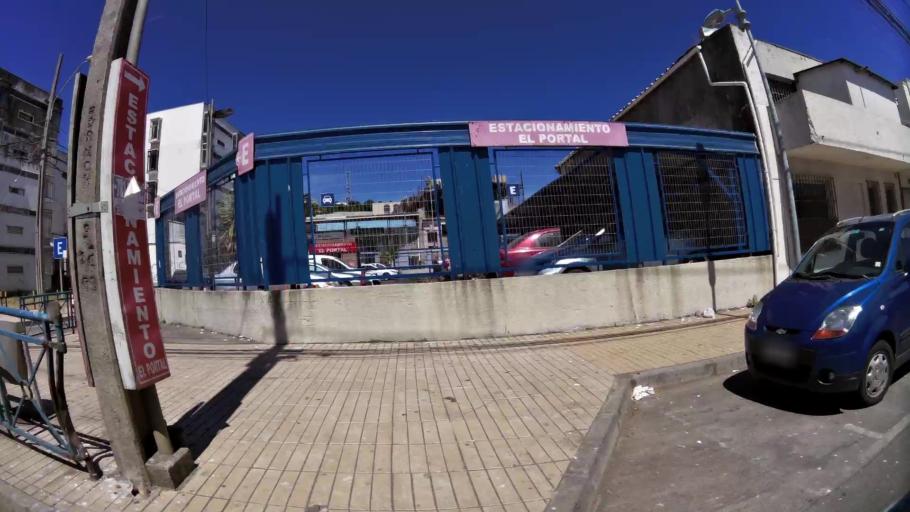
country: CL
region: Biobio
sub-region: Provincia de Concepcion
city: Talcahuano
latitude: -36.7142
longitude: -73.1111
